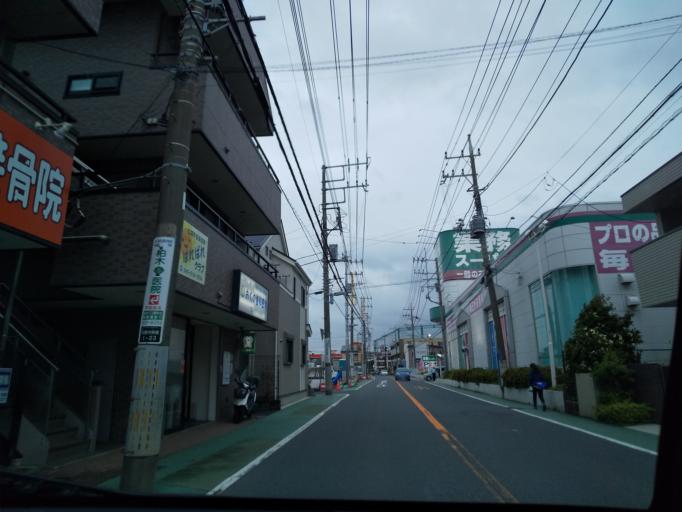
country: JP
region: Kanagawa
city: Fujisawa
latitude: 35.4078
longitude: 139.5008
